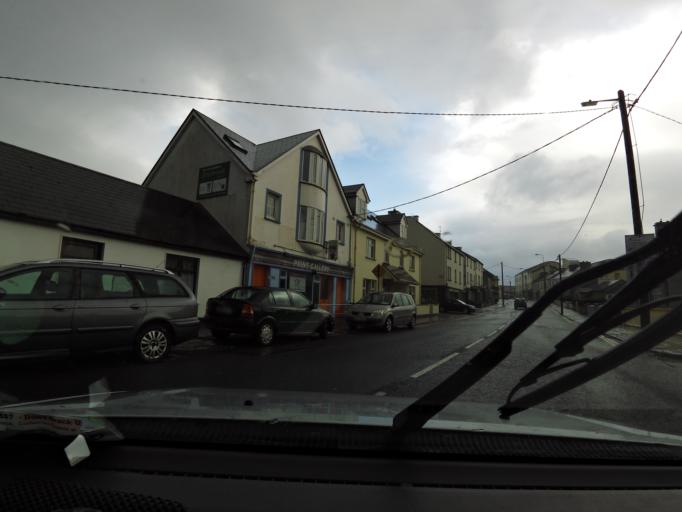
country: IE
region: Munster
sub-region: An Clar
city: Kilrush
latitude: 52.9334
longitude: -9.3447
